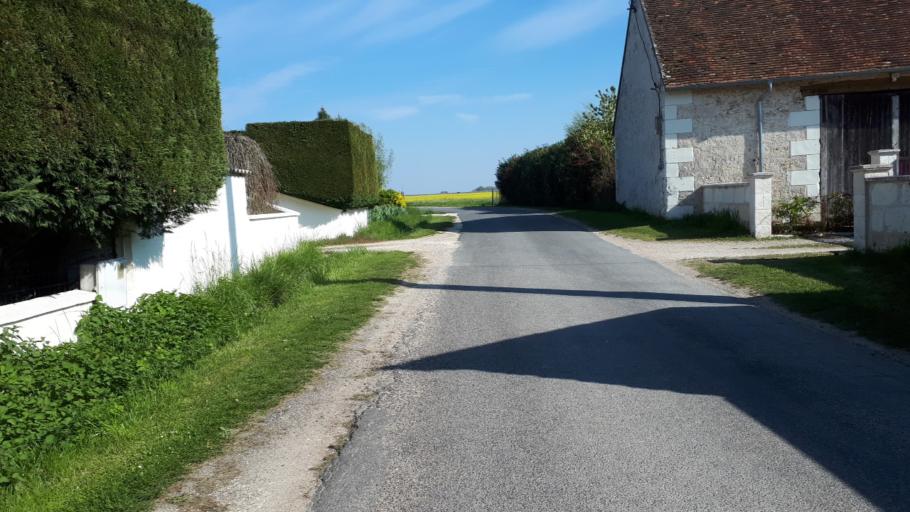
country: FR
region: Centre
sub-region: Departement du Loir-et-Cher
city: Contres
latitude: 47.3830
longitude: 1.3898
